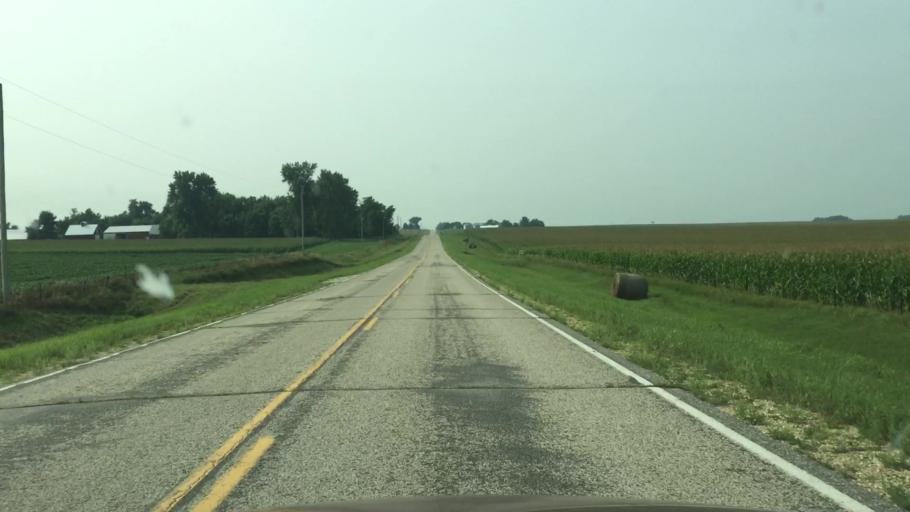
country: US
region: Iowa
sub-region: Osceola County
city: Sibley
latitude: 43.2807
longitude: -95.7829
